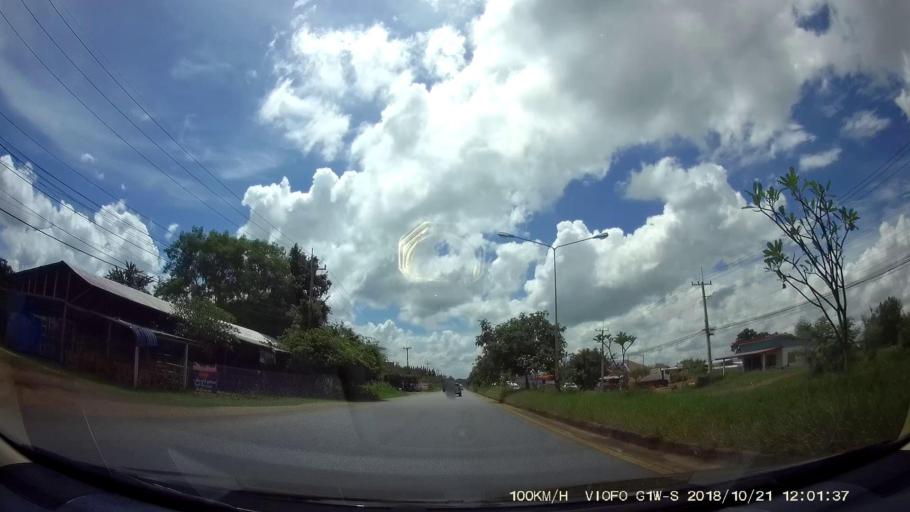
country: TH
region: Chaiyaphum
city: Chatturat
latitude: 15.5358
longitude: 101.8341
